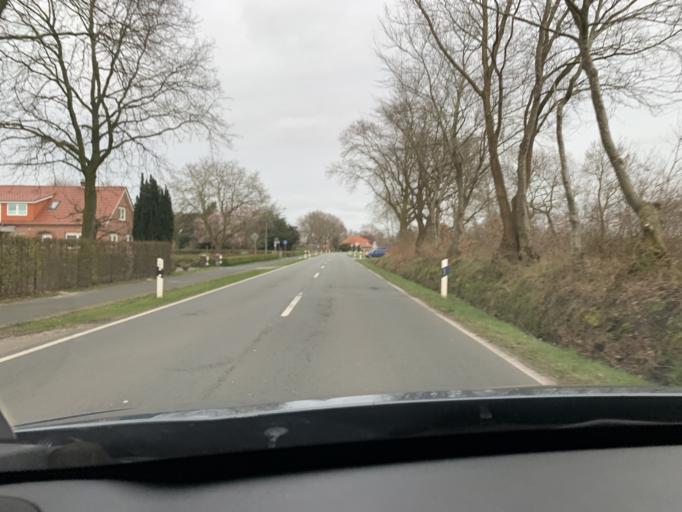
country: DE
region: Lower Saxony
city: Apen
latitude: 53.2293
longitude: 7.7431
